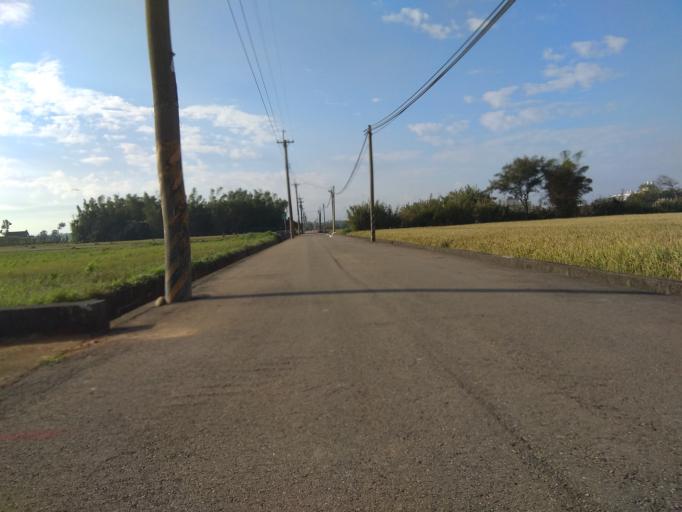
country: TW
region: Taiwan
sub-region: Hsinchu
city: Zhubei
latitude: 24.9805
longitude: 121.0582
